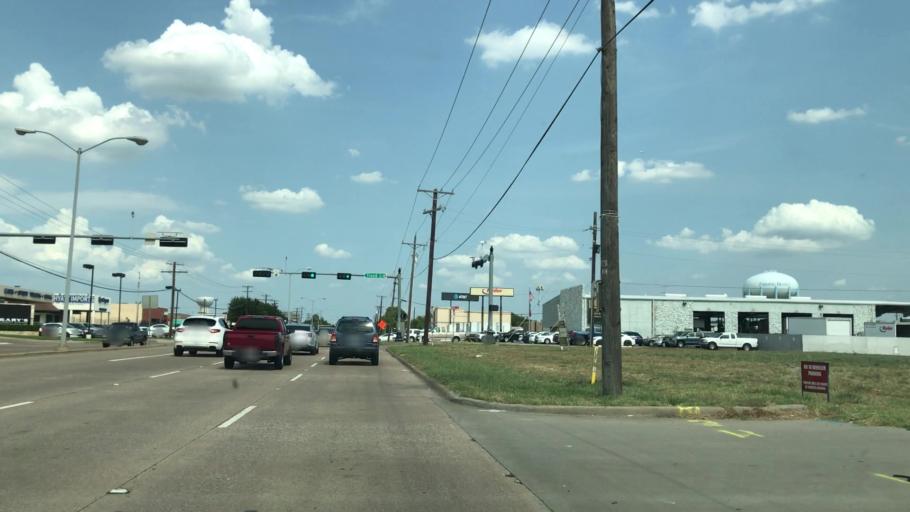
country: US
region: Texas
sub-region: Dallas County
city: Carrollton
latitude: 32.9531
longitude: -96.8619
